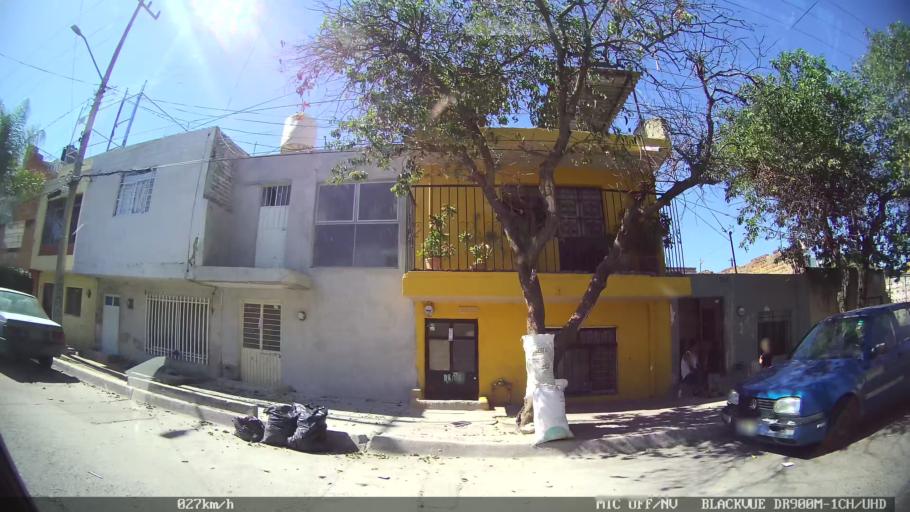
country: MX
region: Jalisco
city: Tlaquepaque
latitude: 20.6538
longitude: -103.2847
